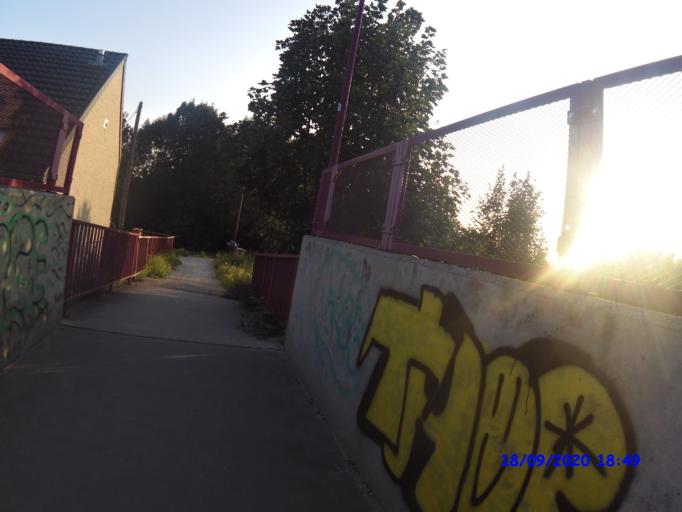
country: BE
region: Wallonia
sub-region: Province de Liege
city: Waremme
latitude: 50.6921
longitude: 5.2584
